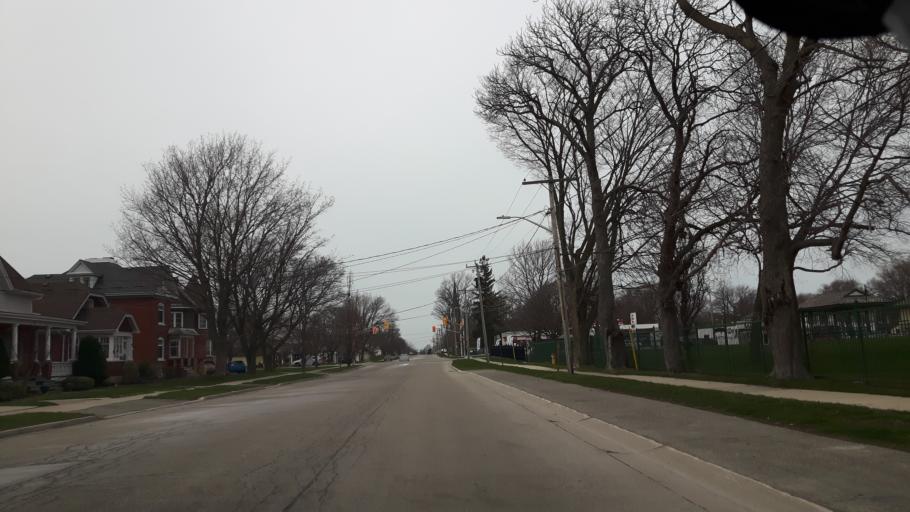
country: CA
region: Ontario
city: Goderich
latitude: 43.7456
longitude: -81.7062
